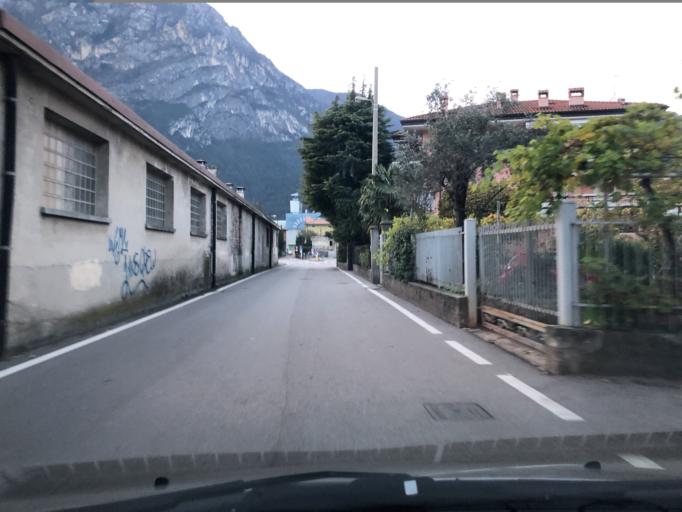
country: IT
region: Trentino-Alto Adige
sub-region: Provincia di Trento
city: Riva del Garda
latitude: 45.8857
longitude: 10.8581
